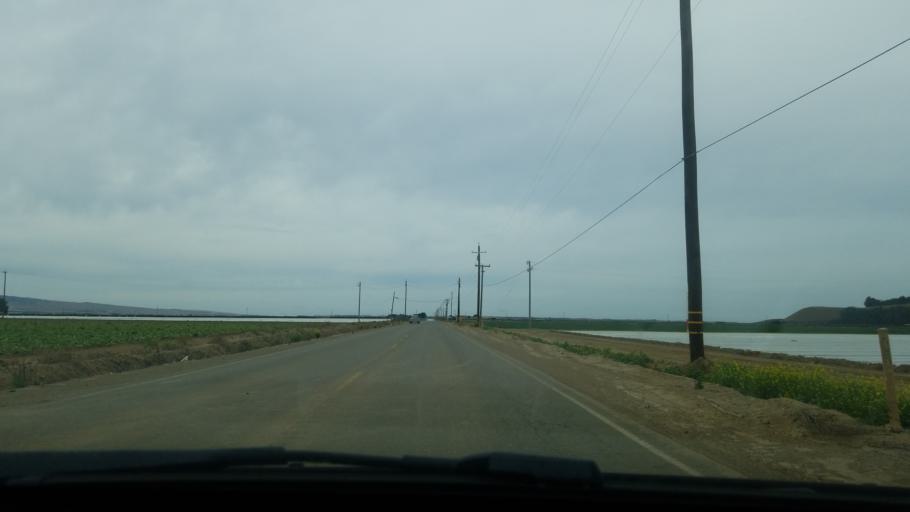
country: US
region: California
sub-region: San Luis Obispo County
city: Nipomo
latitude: 35.0054
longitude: -120.5090
